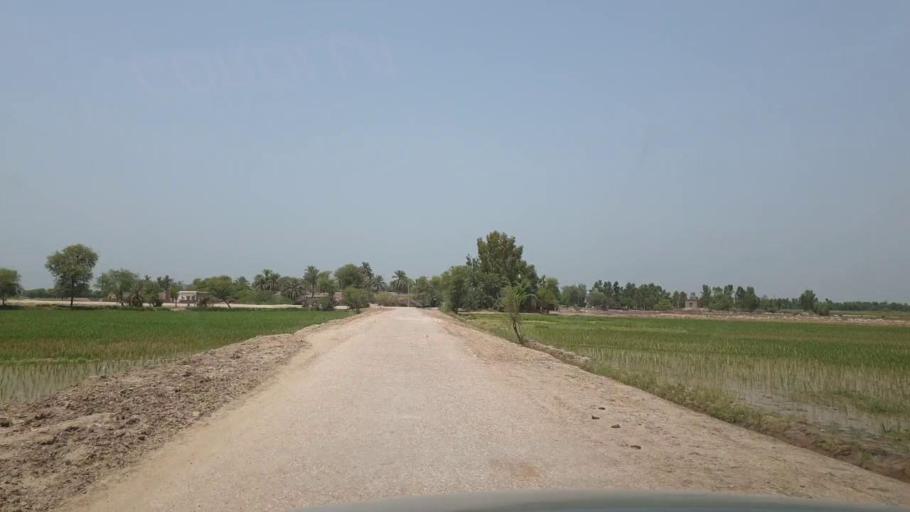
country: PK
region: Sindh
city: Garhi Yasin
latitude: 27.8687
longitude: 68.4560
